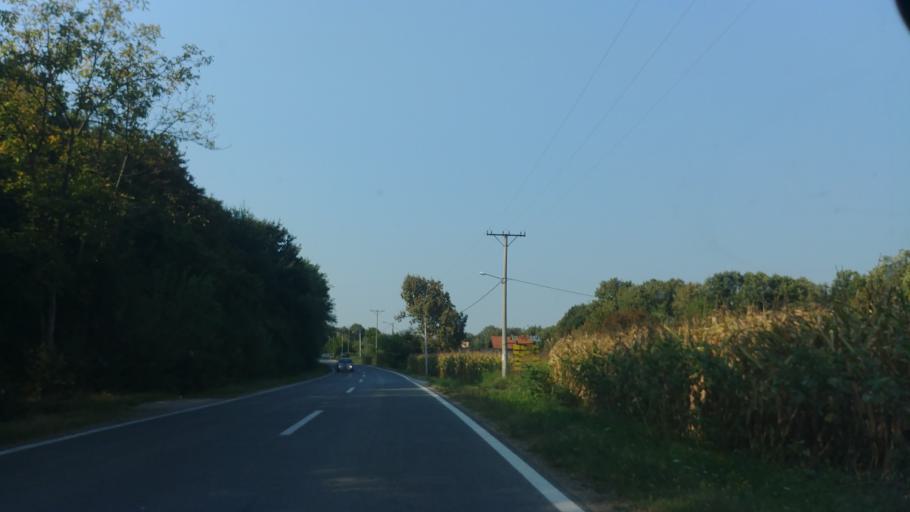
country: BA
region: Brcko
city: Brcko
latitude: 44.7893
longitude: 18.8167
